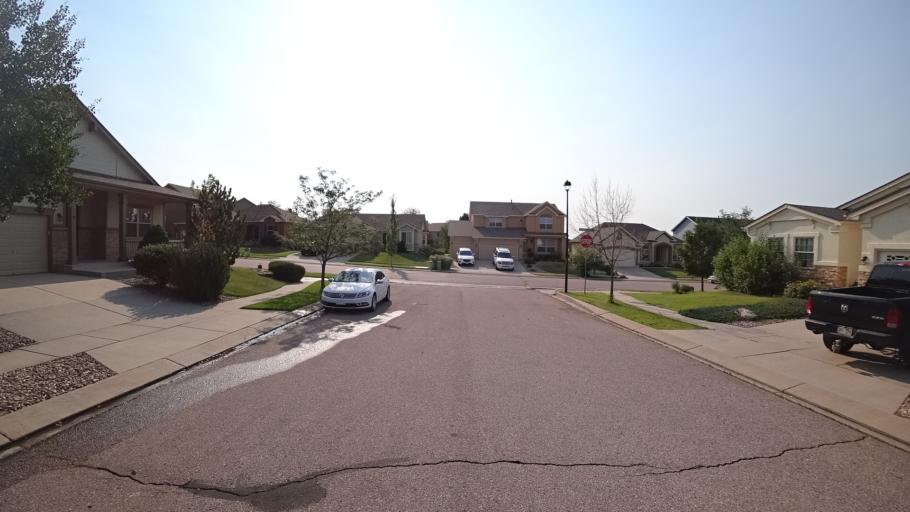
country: US
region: Colorado
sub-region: El Paso County
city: Black Forest
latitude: 38.9556
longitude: -104.7213
